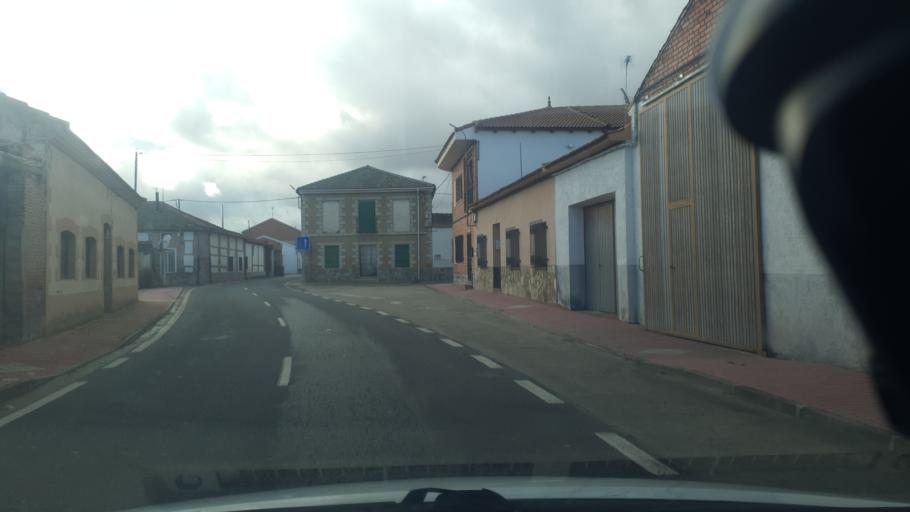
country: ES
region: Castille and Leon
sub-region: Provincia de Segovia
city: Santiuste de San Juan Bautista
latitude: 41.1552
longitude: -4.5700
